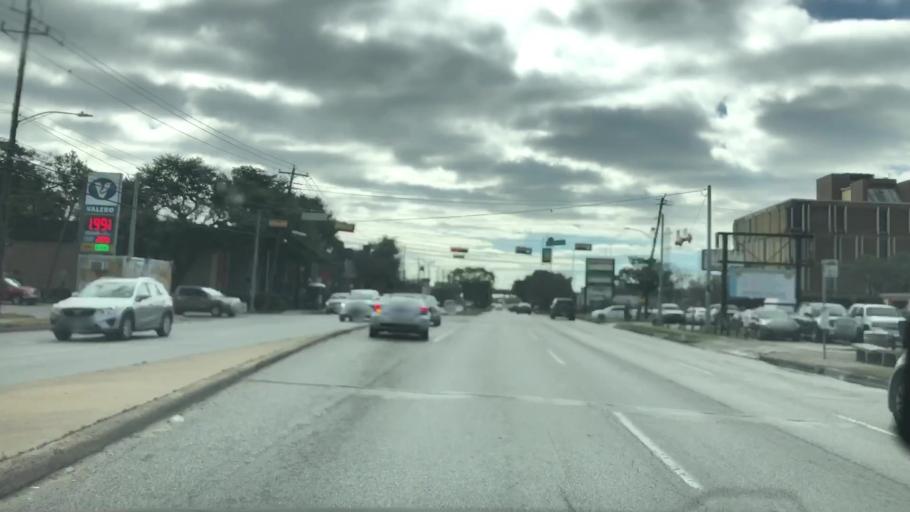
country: US
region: Texas
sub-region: Harris County
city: Piney Point Village
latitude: 29.7262
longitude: -95.5012
